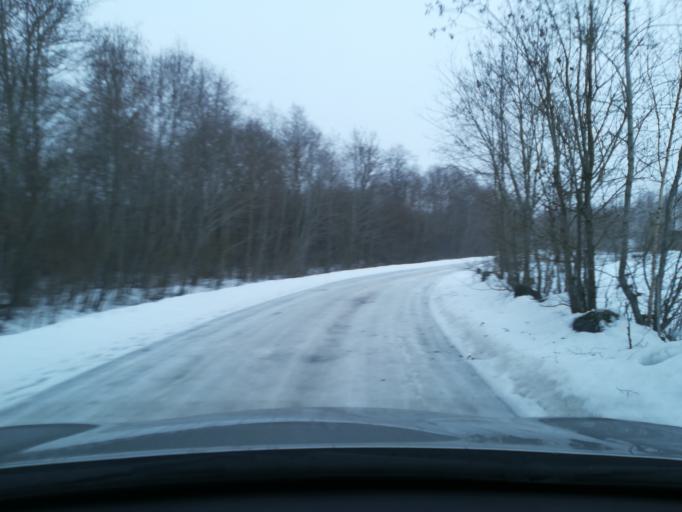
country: EE
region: Harju
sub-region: Rae vald
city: Jueri
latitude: 59.3759
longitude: 24.8760
